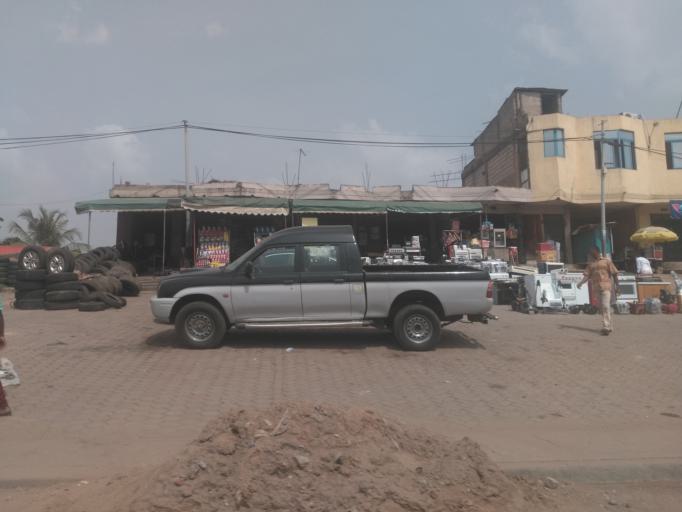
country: GH
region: Greater Accra
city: Dome
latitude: 5.6090
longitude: -0.2405
